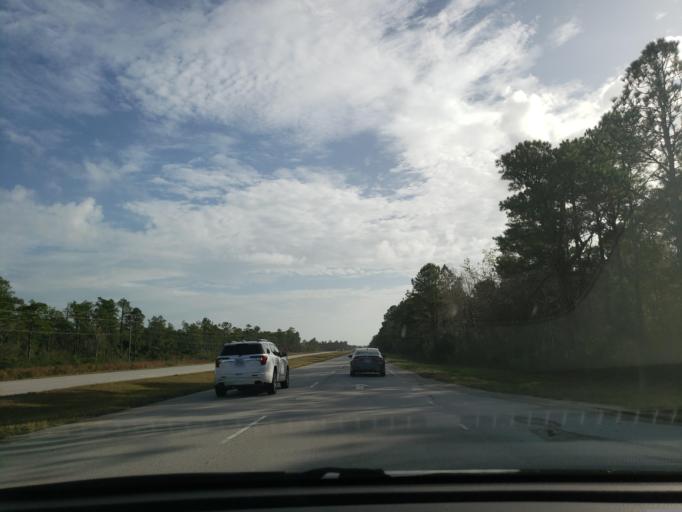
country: US
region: North Carolina
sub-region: Onslow County
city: Sneads Ferry
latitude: 34.6102
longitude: -77.4835
